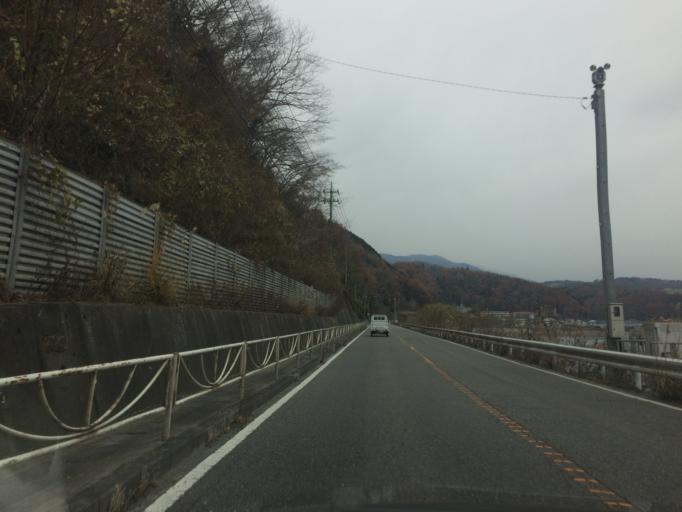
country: JP
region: Yamanashi
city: Ryuo
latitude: 35.4576
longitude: 138.4433
